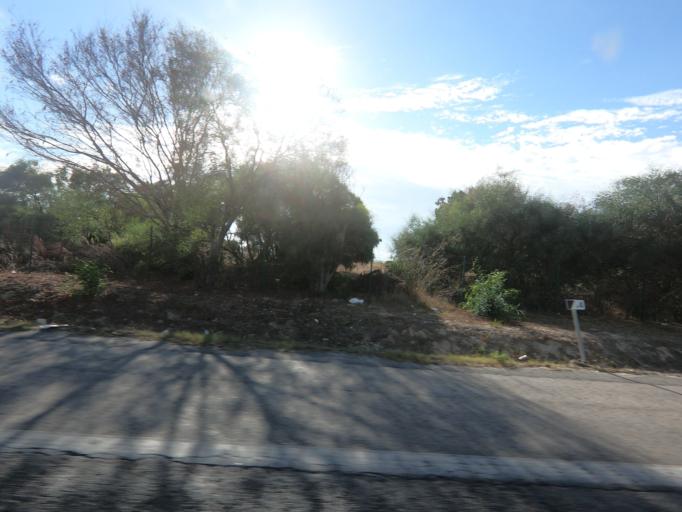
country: PT
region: Setubal
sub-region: Barreiro
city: Santo Antonio da Charneca
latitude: 38.6364
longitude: -9.0451
